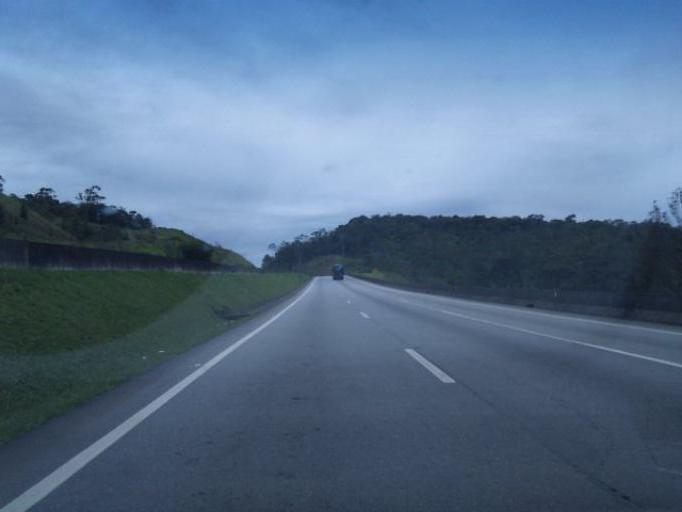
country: BR
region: Sao Paulo
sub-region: Juquitiba
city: Juquitiba
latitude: -24.0096
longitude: -47.1620
